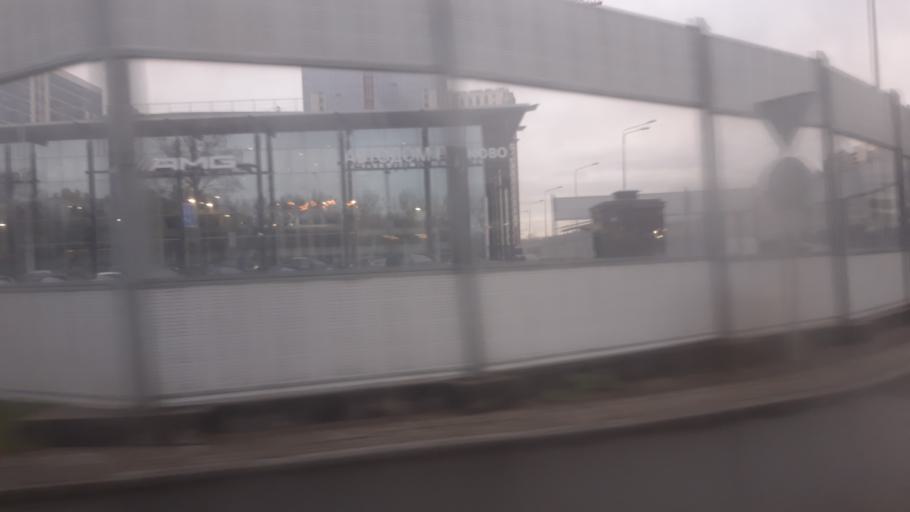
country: RU
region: St.-Petersburg
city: Kupchino
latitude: 59.8311
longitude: 30.3229
